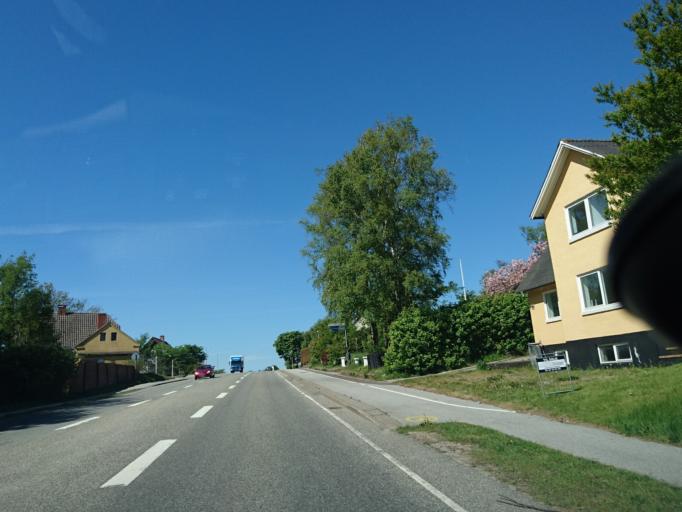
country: DK
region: North Denmark
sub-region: Hjorring Kommune
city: Tars
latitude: 57.4553
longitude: 10.1278
